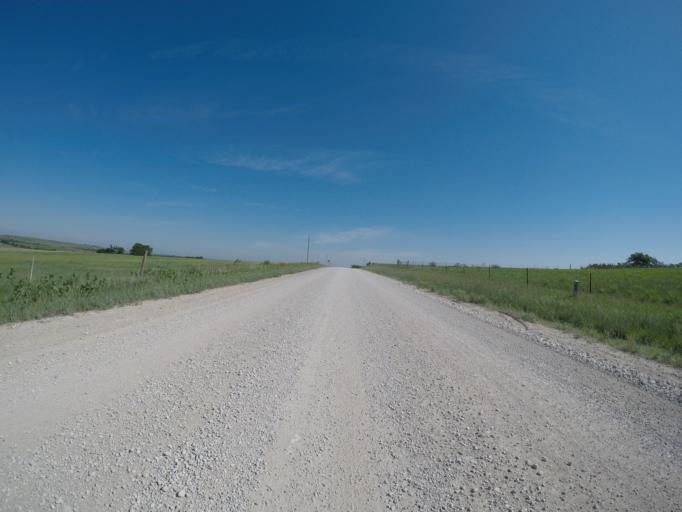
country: US
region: Kansas
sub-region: Wabaunsee County
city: Alma
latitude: 38.9586
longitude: -96.1137
